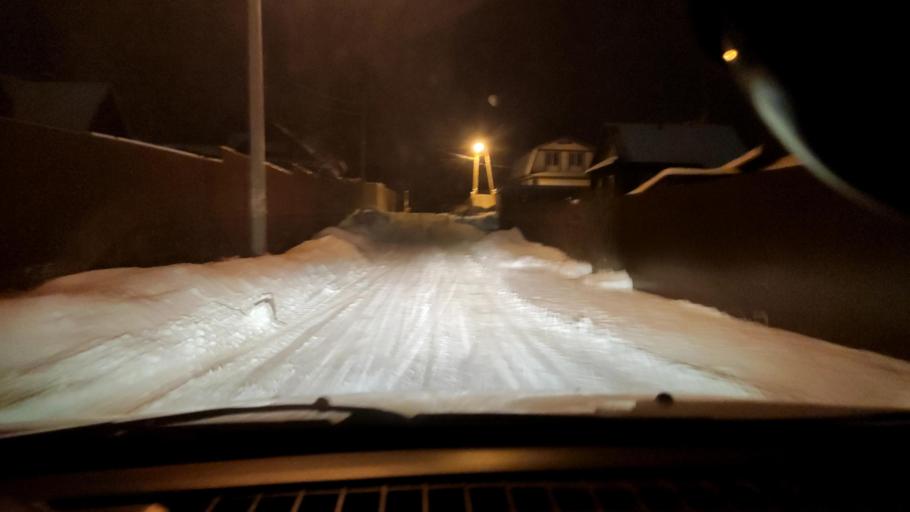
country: RU
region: Perm
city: Perm
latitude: 58.0343
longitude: 56.2530
